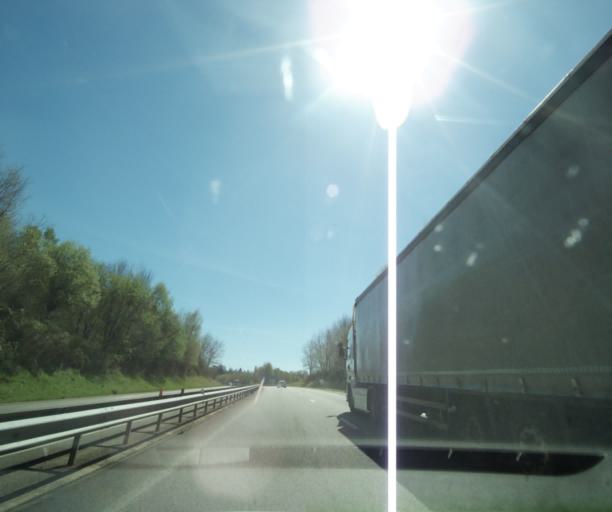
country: FR
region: Limousin
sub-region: Departement de la Haute-Vienne
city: Saint-Germain-les-Belles
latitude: 45.6038
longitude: 1.4470
